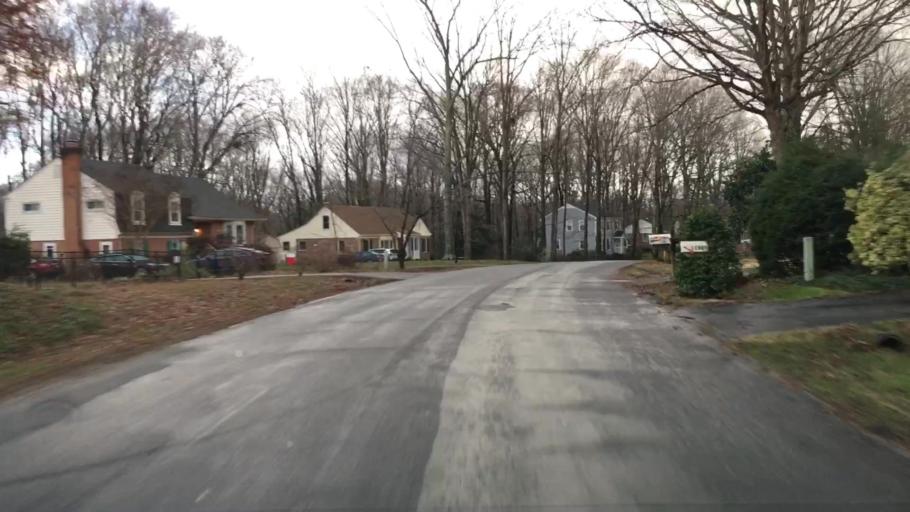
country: US
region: Virginia
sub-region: Chesterfield County
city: Bon Air
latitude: 37.5183
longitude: -77.6248
